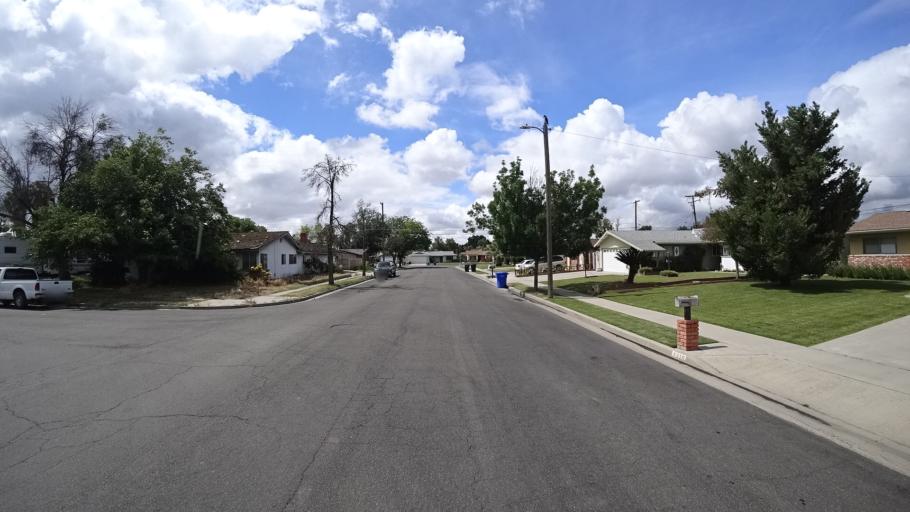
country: US
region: California
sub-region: Kings County
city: Hanford
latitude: 36.3405
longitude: -119.6635
